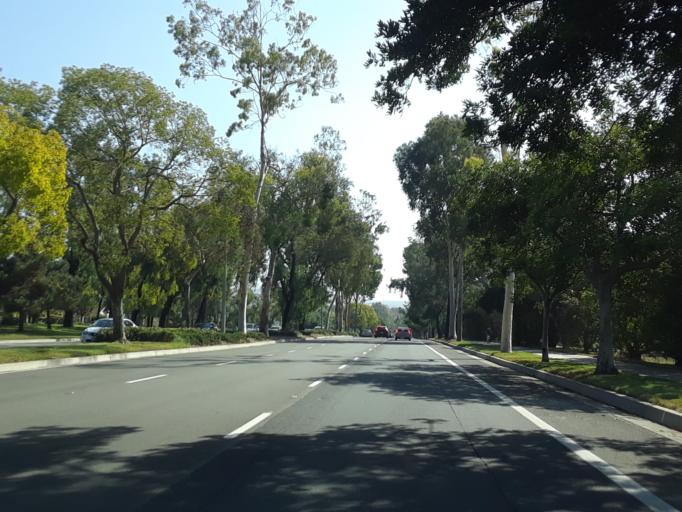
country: US
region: California
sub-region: Orange County
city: Irvine
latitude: 33.6608
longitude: -117.8278
